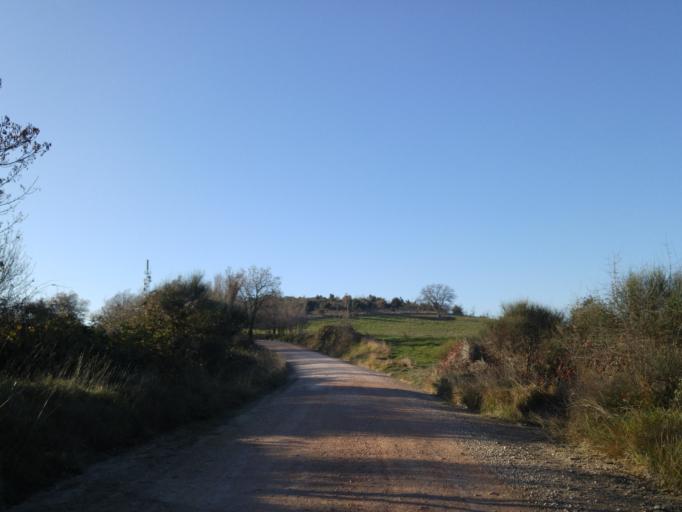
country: IT
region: The Marches
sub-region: Provincia di Pesaro e Urbino
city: Isola del Piano
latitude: 43.7715
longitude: 12.8105
